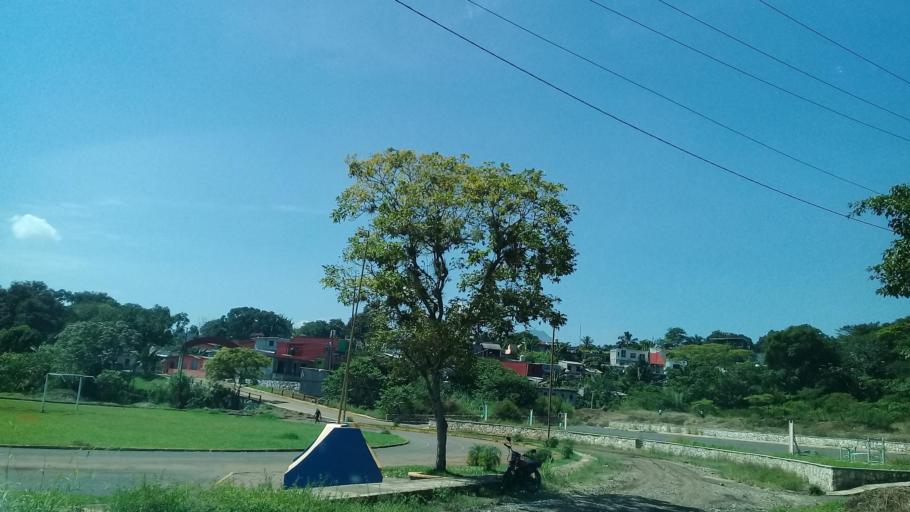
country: MX
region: Veracruz
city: Amatlan de los Reyes
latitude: 18.8431
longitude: -96.9099
